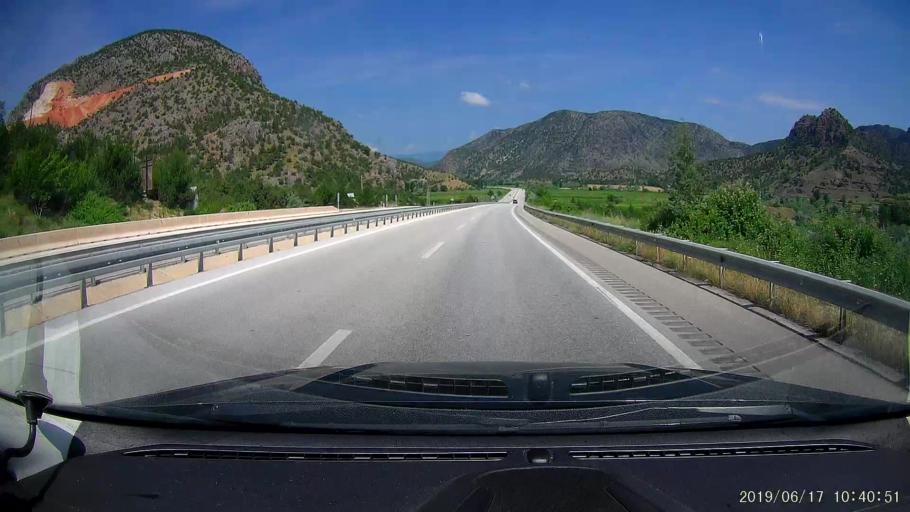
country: TR
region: Corum
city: Kargi
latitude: 41.0304
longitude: 34.5882
